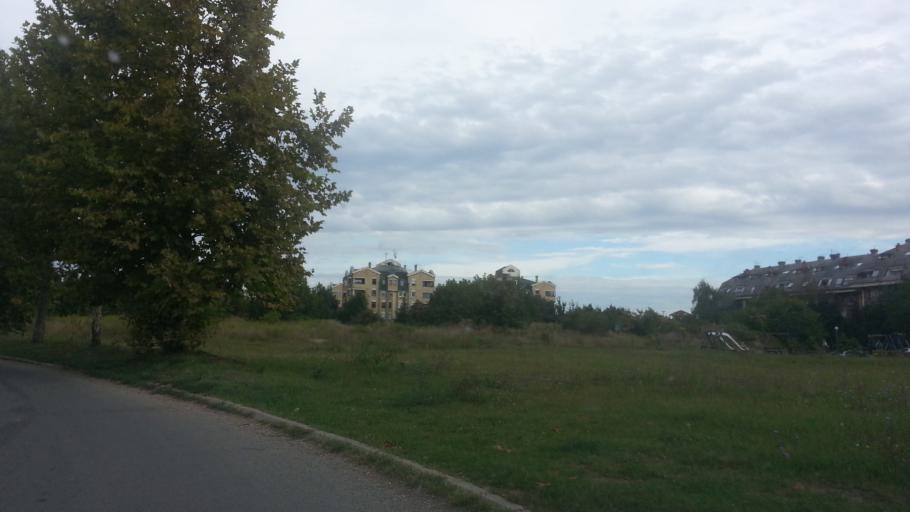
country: RS
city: Novi Banovci
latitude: 44.9666
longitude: 20.2782
